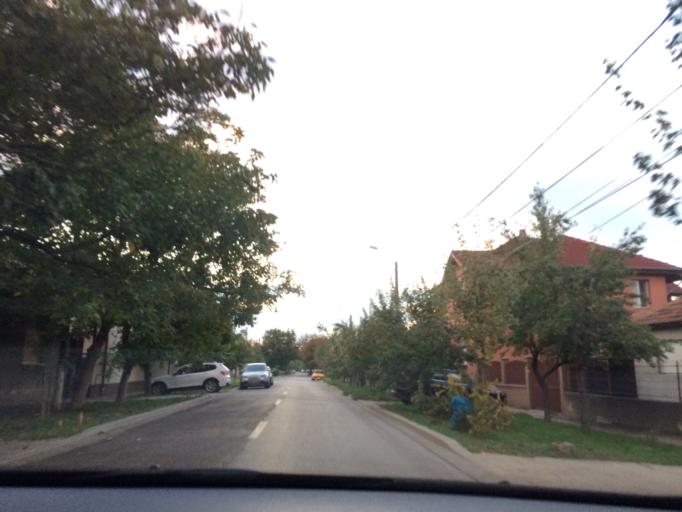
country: RO
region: Timis
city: Timisoara
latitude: 45.7645
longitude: 21.2010
